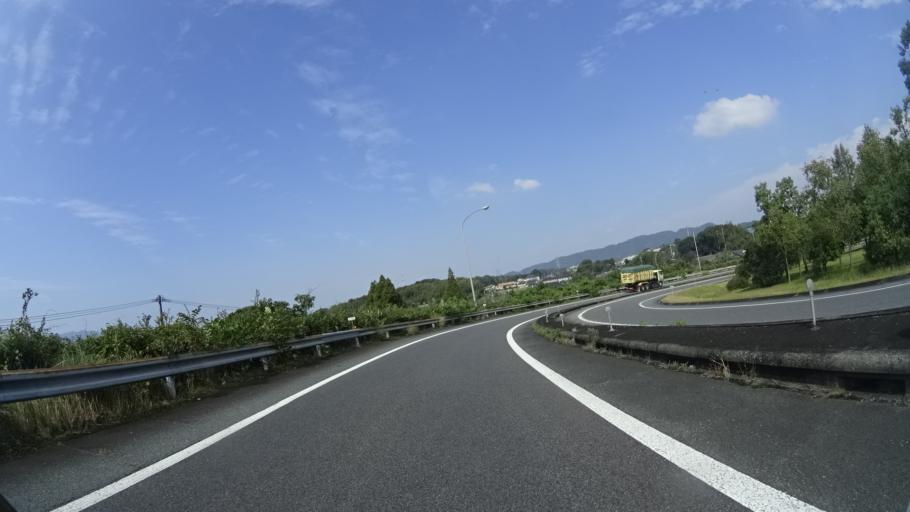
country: JP
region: Kumamoto
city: Matsubase
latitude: 32.6474
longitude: 130.7068
